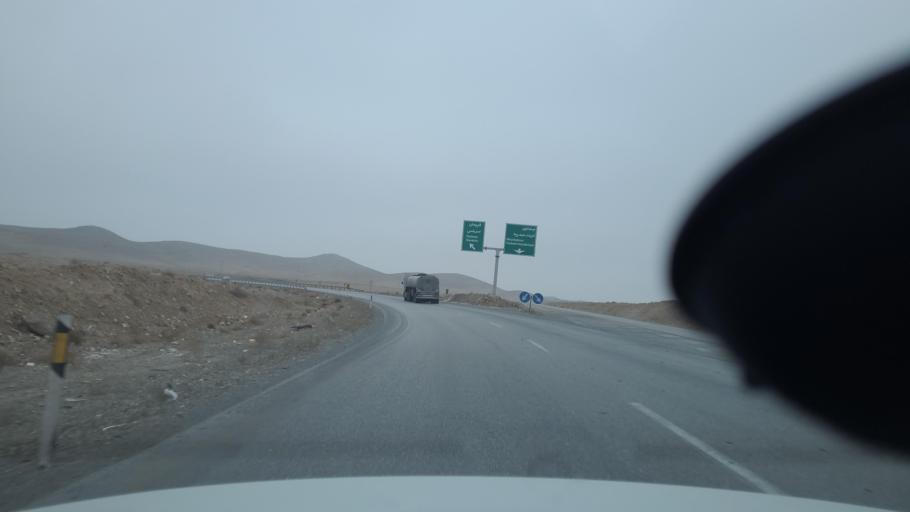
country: IR
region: Razavi Khorasan
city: Fariman
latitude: 35.9926
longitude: 59.7446
